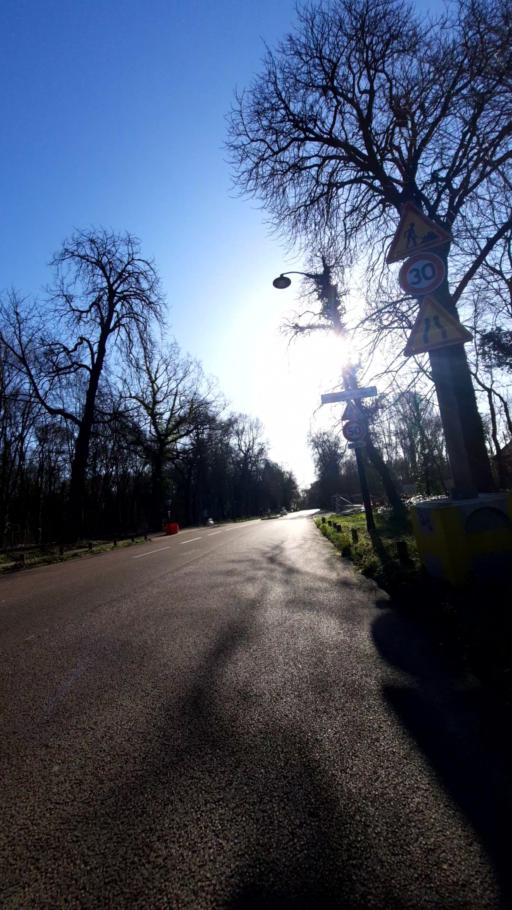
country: FR
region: Ile-de-France
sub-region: Departement du Val-de-Marne
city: Saint-Maurice
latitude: 48.8221
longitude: 2.4323
